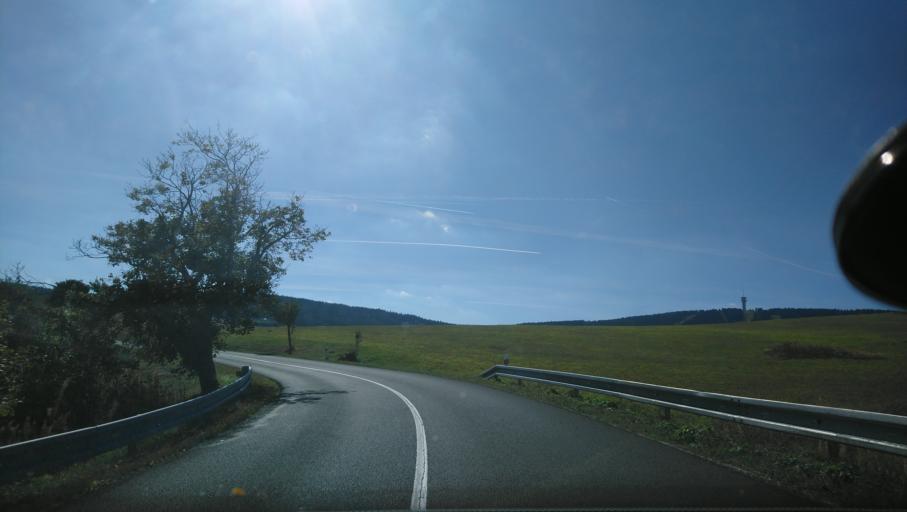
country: DE
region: Saxony
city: Kurort Oberwiesenthal
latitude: 50.4141
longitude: 12.9896
